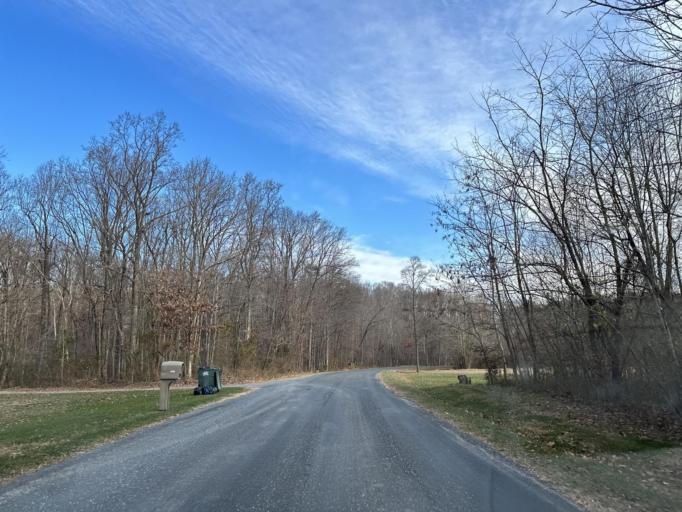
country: US
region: Virginia
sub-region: City of Staunton
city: Staunton
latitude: 38.2150
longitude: -79.2179
